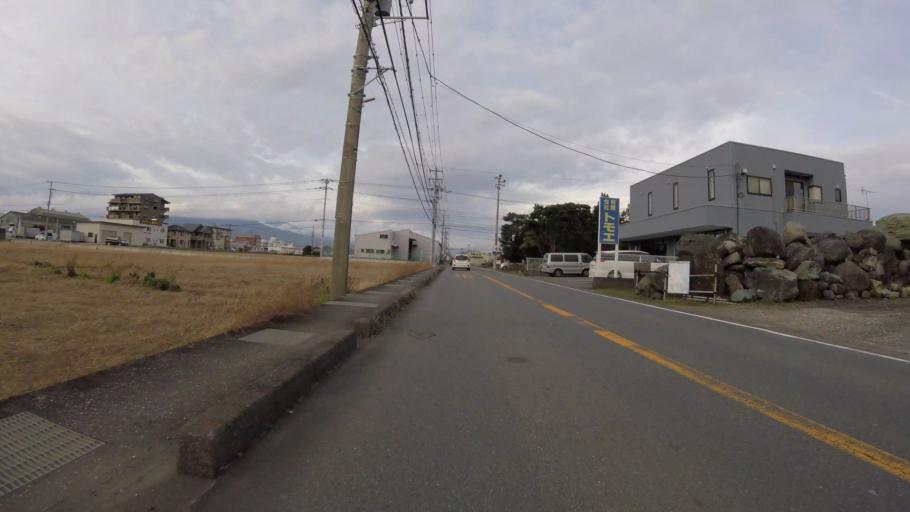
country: JP
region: Shizuoka
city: Mishima
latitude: 35.0926
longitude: 138.9118
